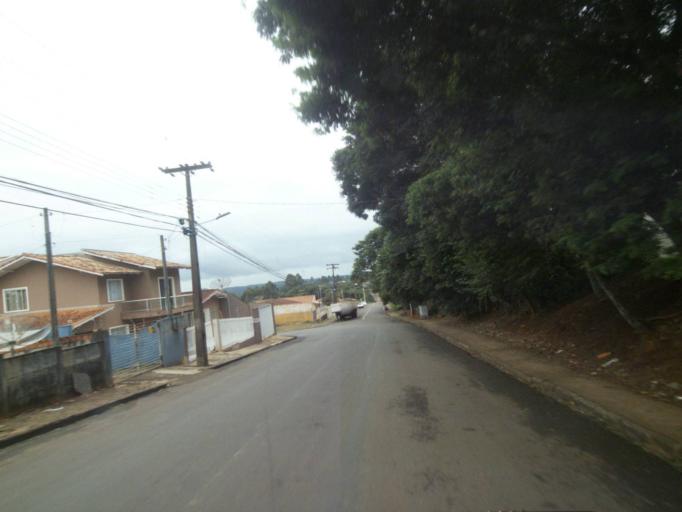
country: BR
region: Parana
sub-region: Telemaco Borba
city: Telemaco Borba
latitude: -24.3235
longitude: -50.6545
